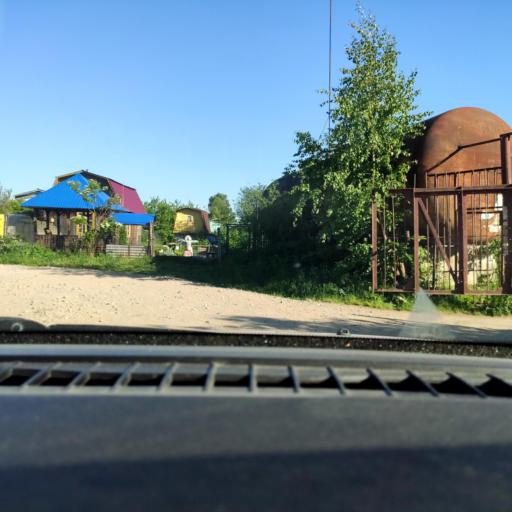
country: RU
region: Perm
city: Overyata
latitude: 58.1231
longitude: 55.8740
